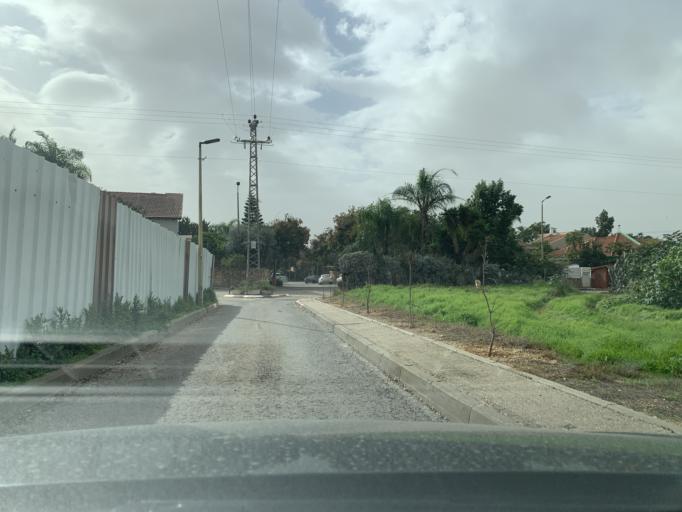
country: IL
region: Central District
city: Jaljulya
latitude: 32.1589
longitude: 34.9418
